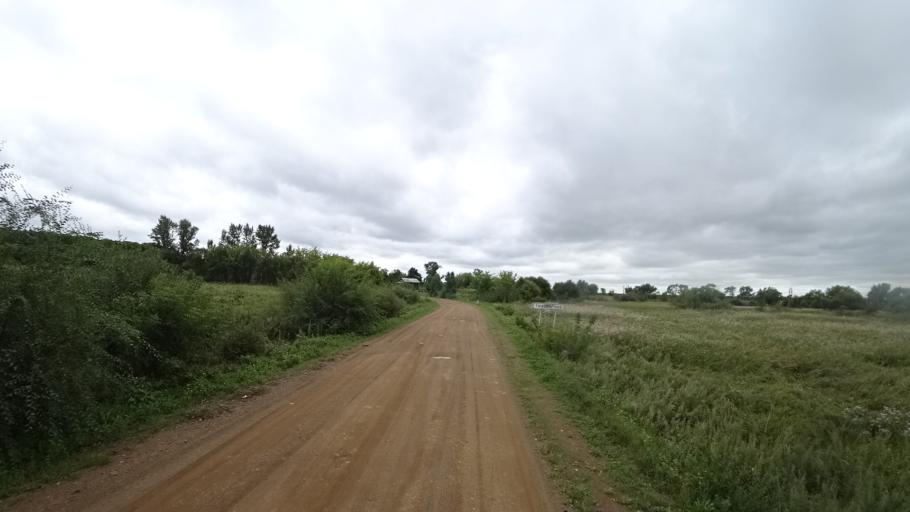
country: RU
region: Primorskiy
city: Chernigovka
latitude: 44.4441
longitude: 132.5729
